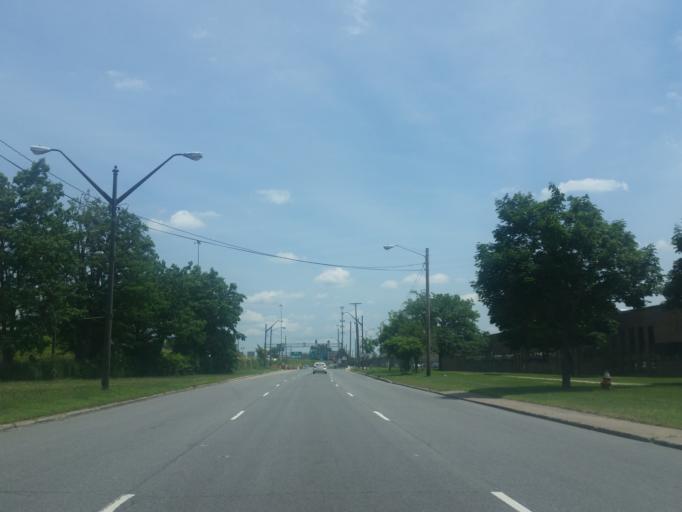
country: US
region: Ohio
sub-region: Cuyahoga County
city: Cleveland
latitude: 41.4910
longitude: -81.6719
